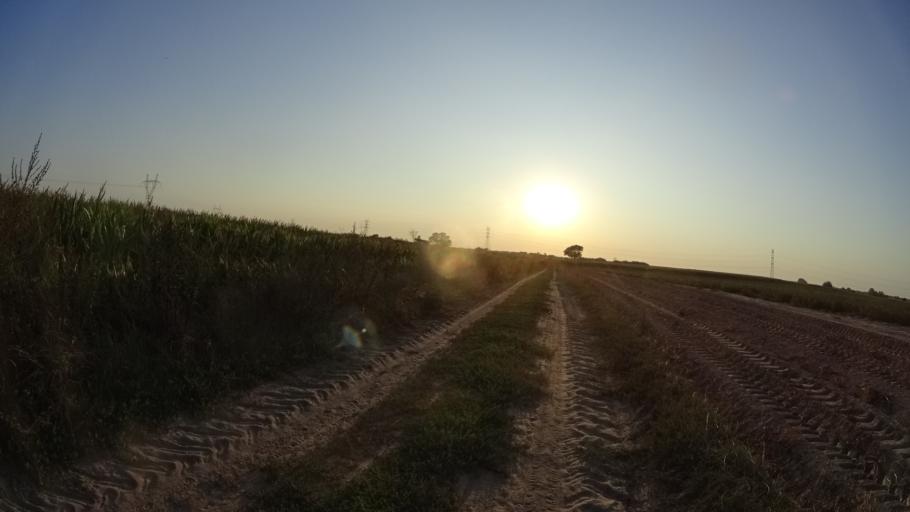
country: PL
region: Masovian Voivodeship
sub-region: Powiat warszawski zachodni
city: Ozarow Mazowiecki
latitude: 52.2401
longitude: 20.7796
